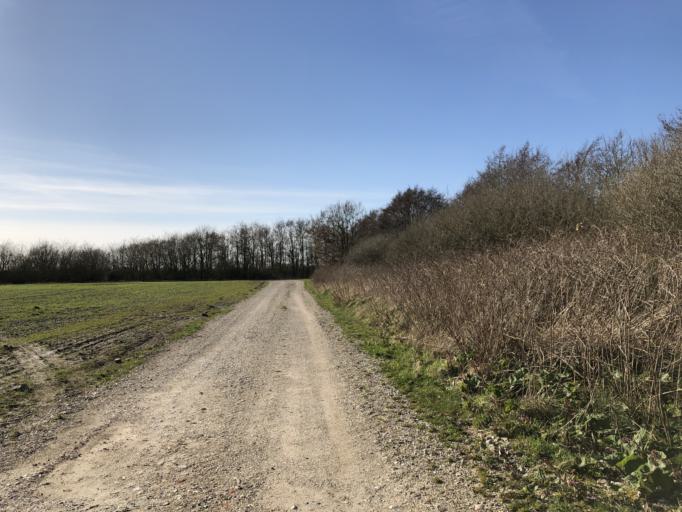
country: DK
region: Central Jutland
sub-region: Holstebro Kommune
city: Ulfborg
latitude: 56.3251
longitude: 8.3293
